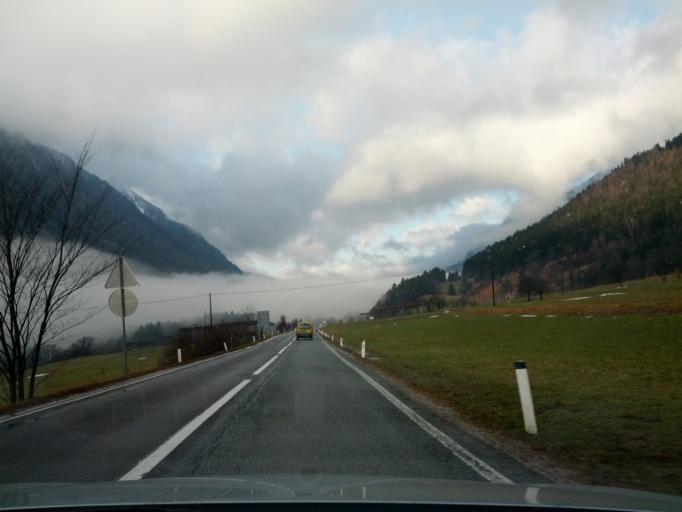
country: SI
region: Jesenice
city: Hrusica
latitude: 46.4652
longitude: 13.9420
